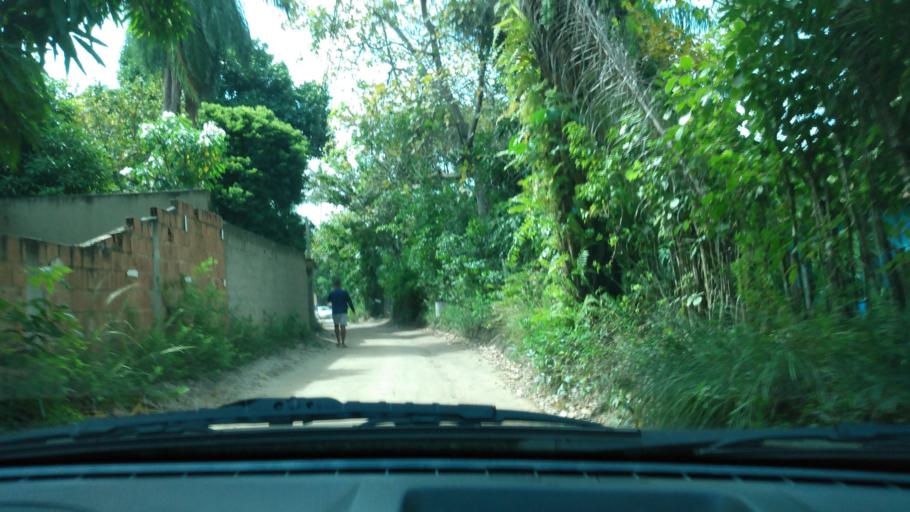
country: BR
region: Pernambuco
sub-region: Cabo De Santo Agostinho
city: Cabo
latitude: -8.3529
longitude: -34.9641
